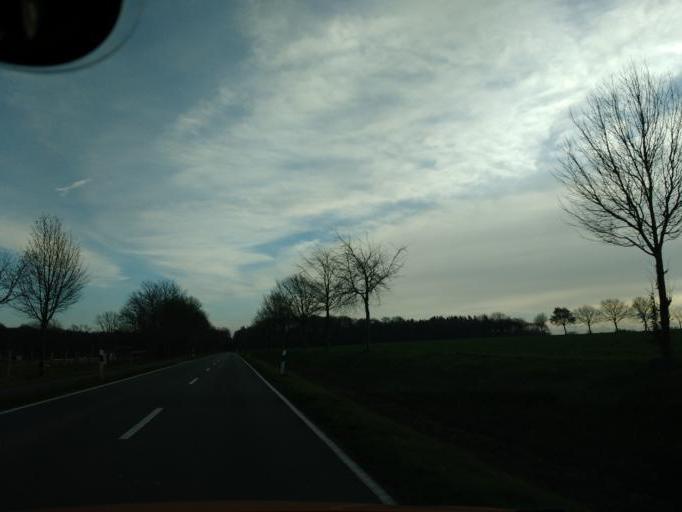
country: DE
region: Lower Saxony
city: Hude
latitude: 53.1210
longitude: 8.4385
